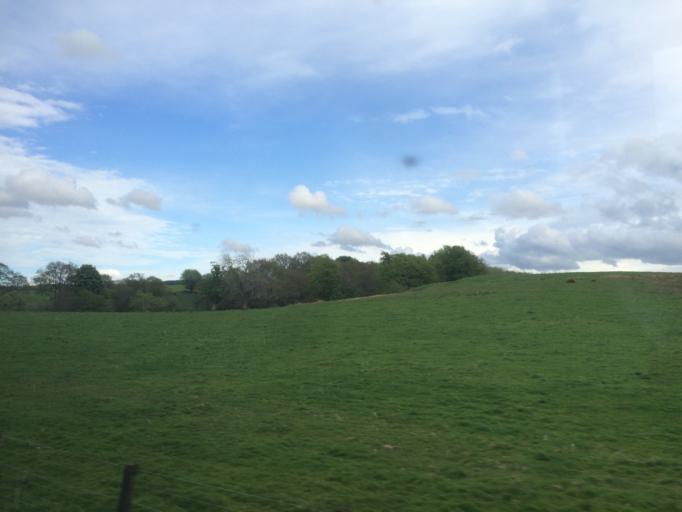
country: GB
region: Scotland
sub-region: Stirling
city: Dunblane
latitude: 56.2325
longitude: -3.9168
